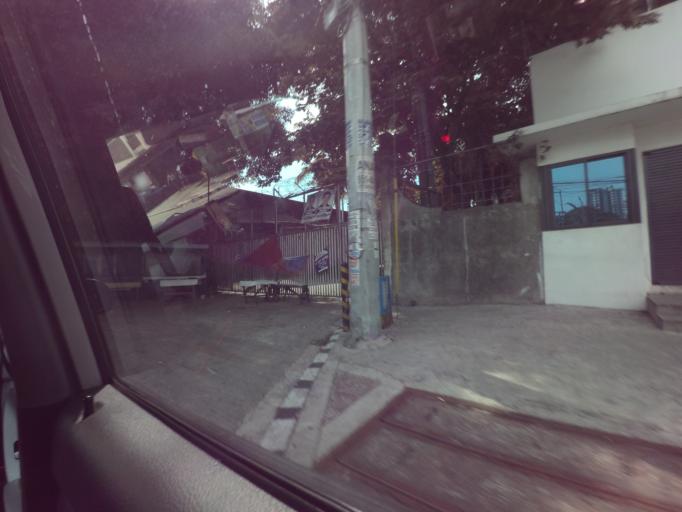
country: PH
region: Metro Manila
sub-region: San Juan
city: San Juan
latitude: 14.6074
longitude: 121.0152
